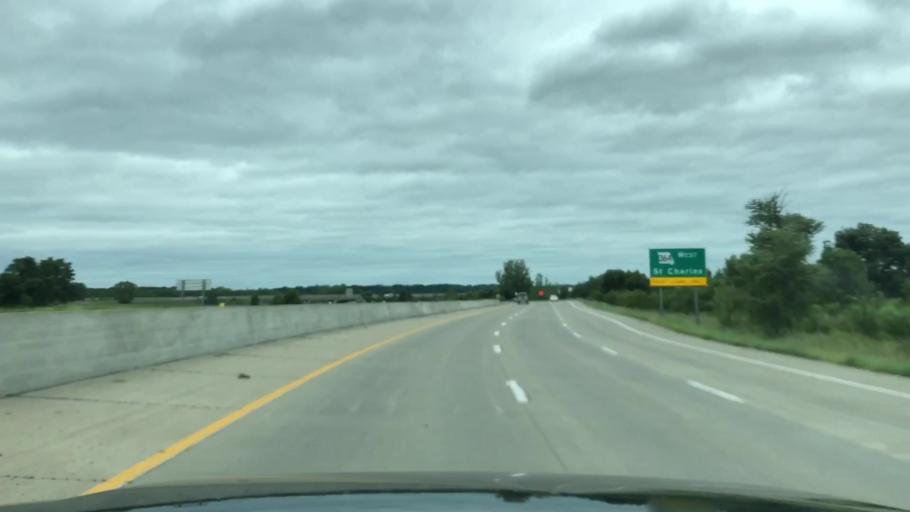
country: US
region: Missouri
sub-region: Saint Louis County
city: Maryland Heights
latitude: 38.7144
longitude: -90.4998
